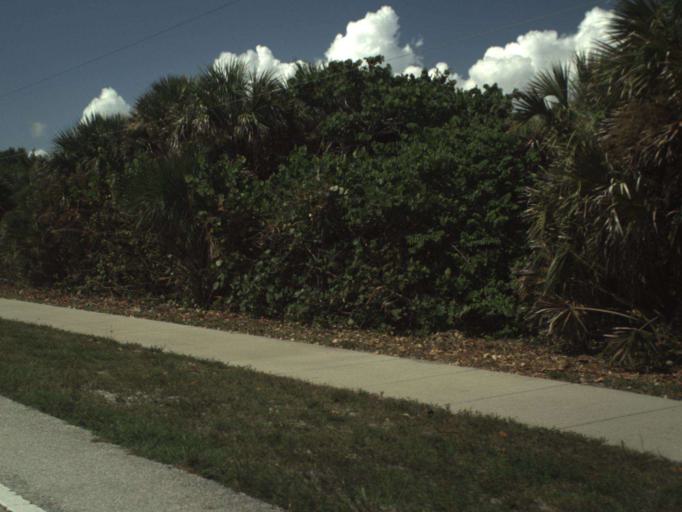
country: US
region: Florida
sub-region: Indian River County
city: Sebastian
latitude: 27.8481
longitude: -80.4423
